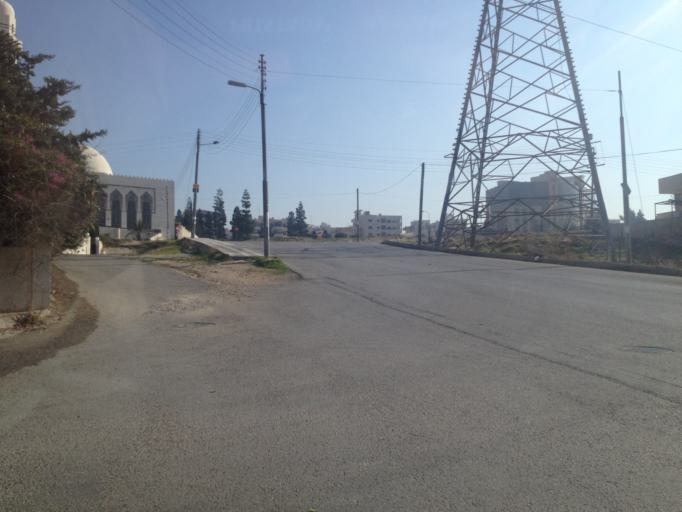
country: JO
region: Amman
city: Wadi as Sir
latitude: 31.9478
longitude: 35.8577
